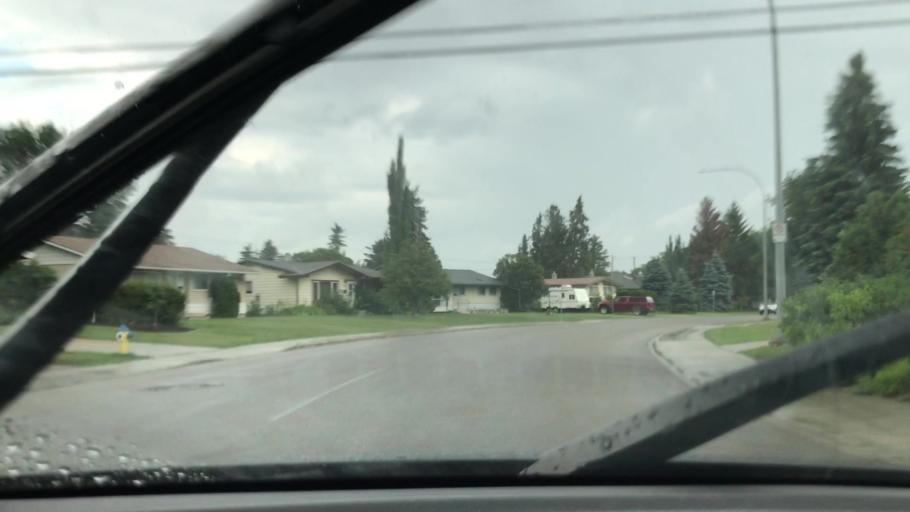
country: CA
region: Alberta
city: Edmonton
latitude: 53.5435
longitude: -113.4294
